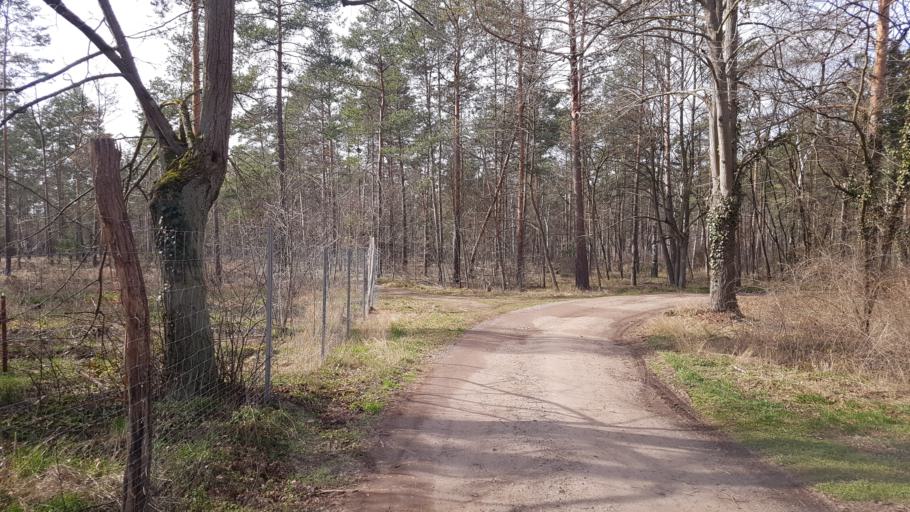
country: DE
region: Brandenburg
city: Doberlug-Kirchhain
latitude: 51.6249
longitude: 13.6149
